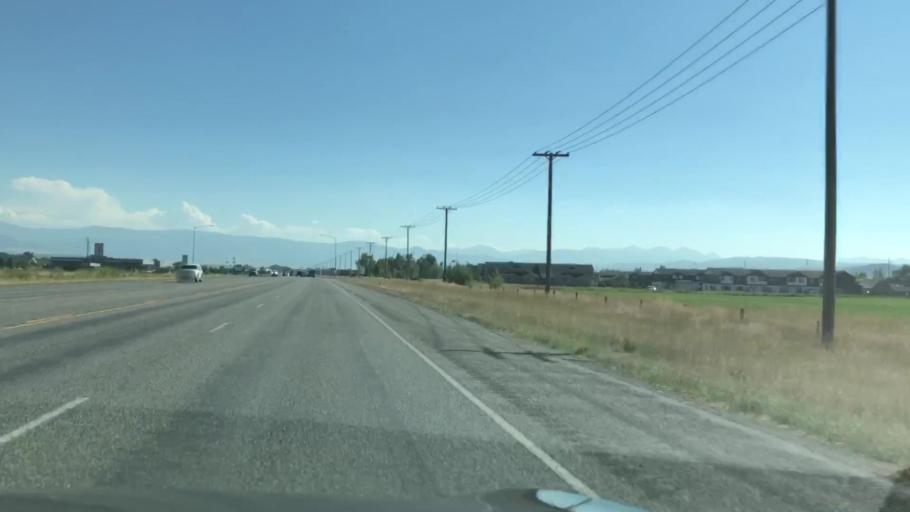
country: US
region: Montana
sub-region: Gallatin County
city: Four Corners
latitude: 45.6876
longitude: -111.1859
